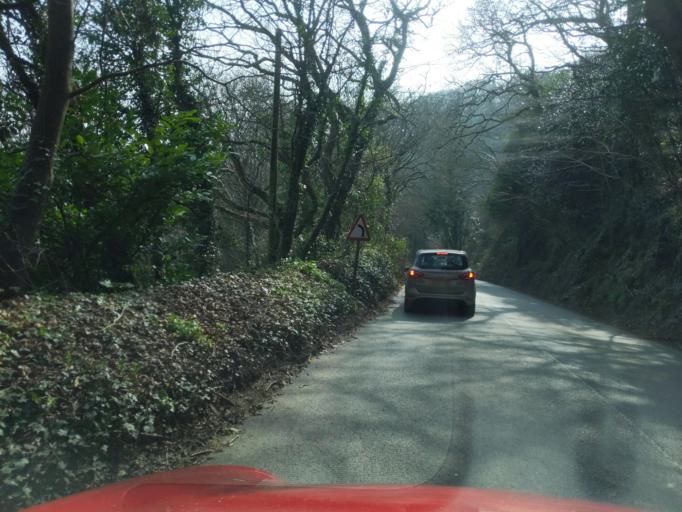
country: GB
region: England
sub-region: Devon
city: Kingsbridge
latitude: 50.3155
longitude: -3.8010
